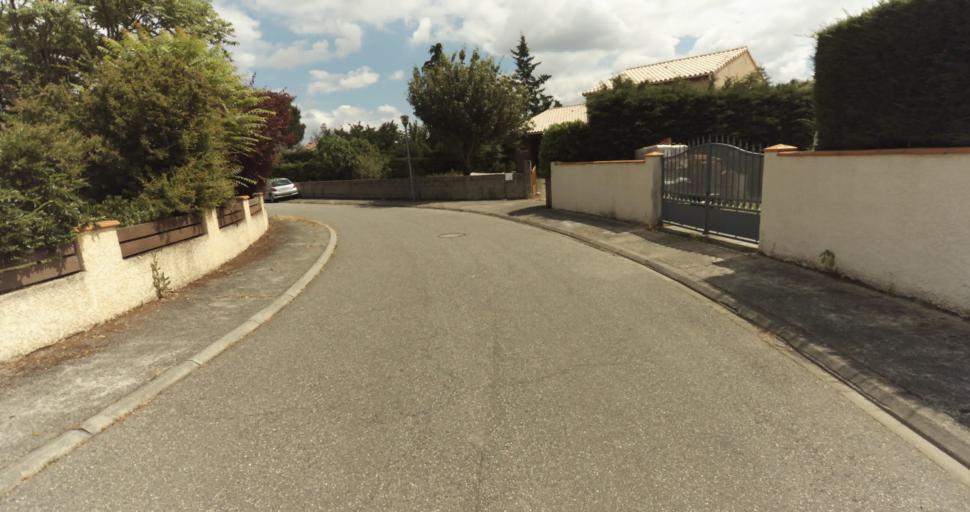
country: FR
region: Midi-Pyrenees
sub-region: Departement de la Haute-Garonne
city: Fontenilles
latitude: 43.5567
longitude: 1.1836
